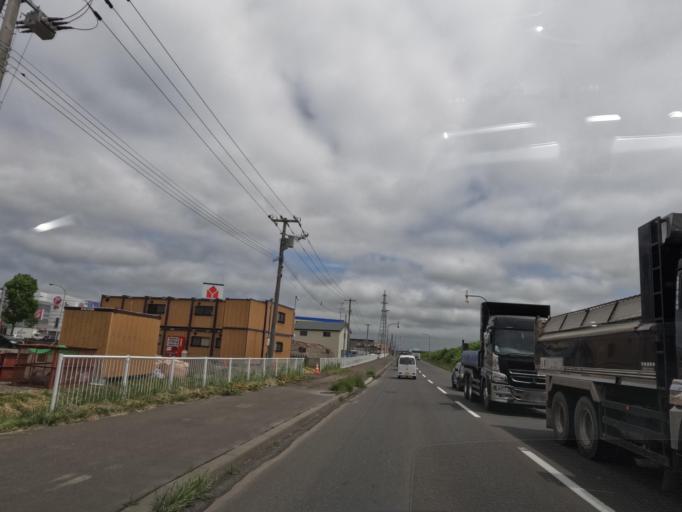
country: JP
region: Hokkaido
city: Sapporo
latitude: 43.0785
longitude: 141.4061
